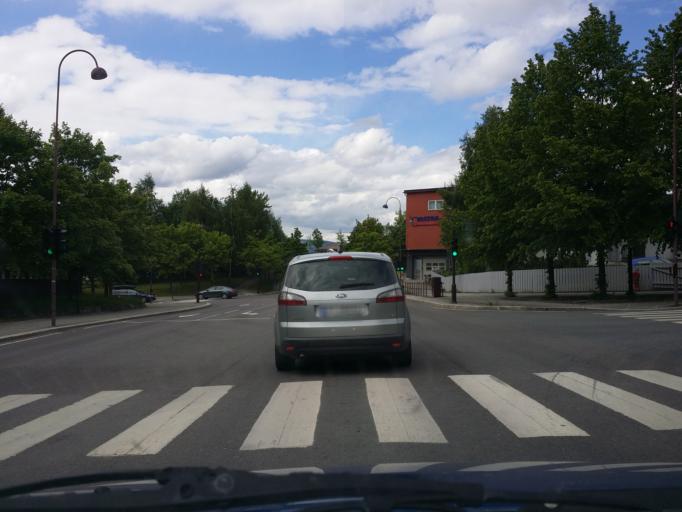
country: NO
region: Oppland
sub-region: Lillehammer
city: Lillehammer
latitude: 61.1132
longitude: 10.4646
